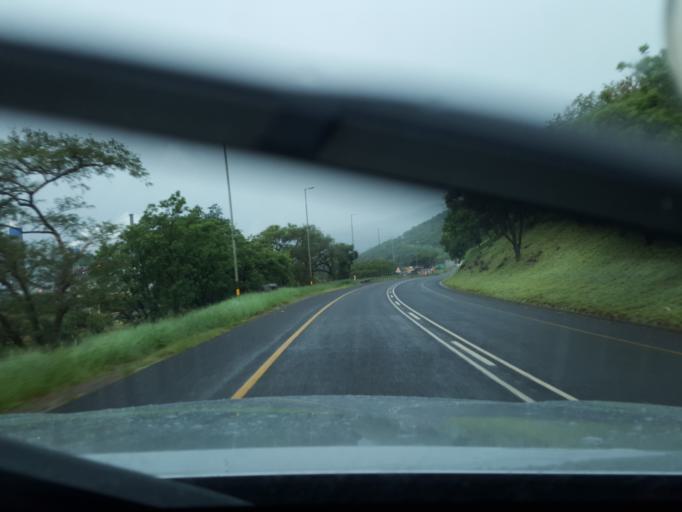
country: ZA
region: Mpumalanga
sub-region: Ehlanzeni District
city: Nelspruit
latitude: -25.5827
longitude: 30.6518
